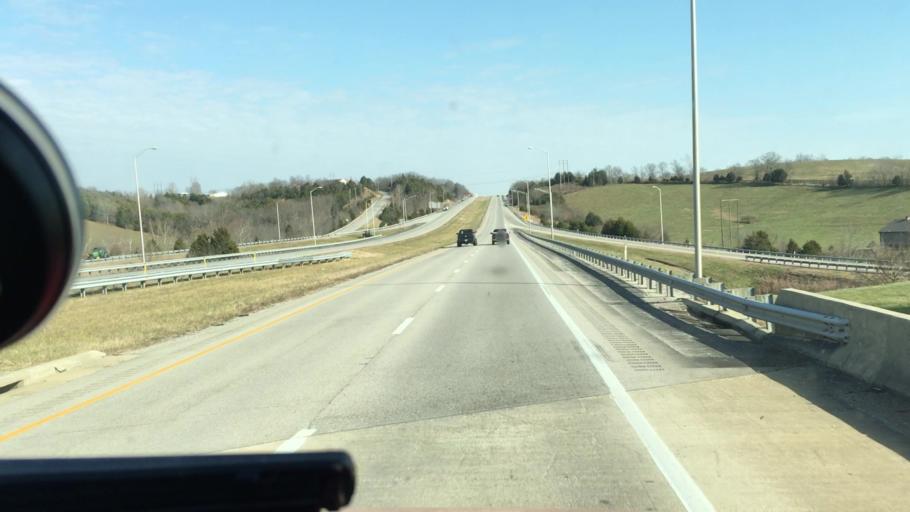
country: US
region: Kentucky
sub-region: Bath County
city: Owingsville
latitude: 38.1397
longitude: -83.7221
